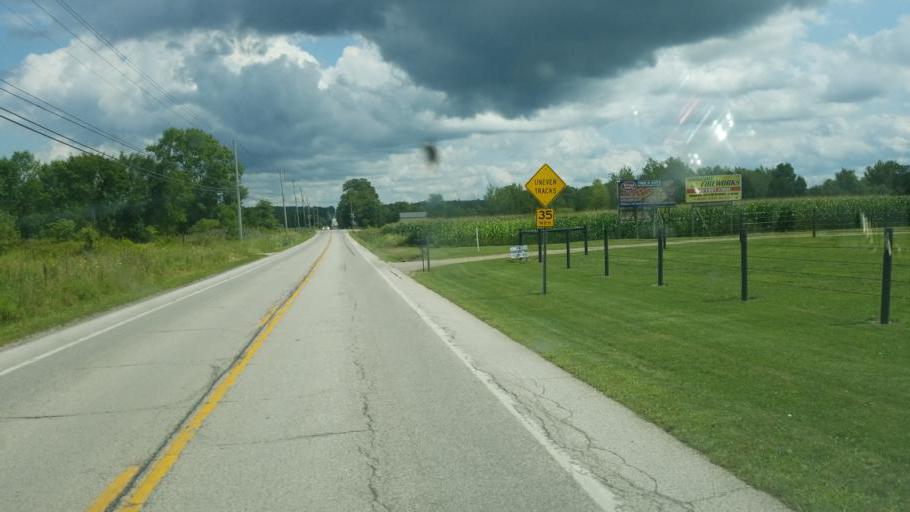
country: US
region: Ohio
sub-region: Ashtabula County
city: Andover
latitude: 41.6069
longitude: -80.6399
